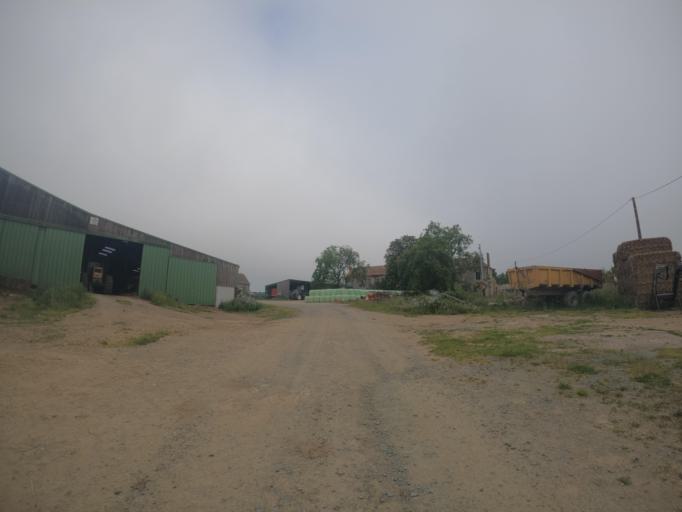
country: FR
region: Poitou-Charentes
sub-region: Departement des Deux-Sevres
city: Chiche
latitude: 46.8957
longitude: -0.3447
